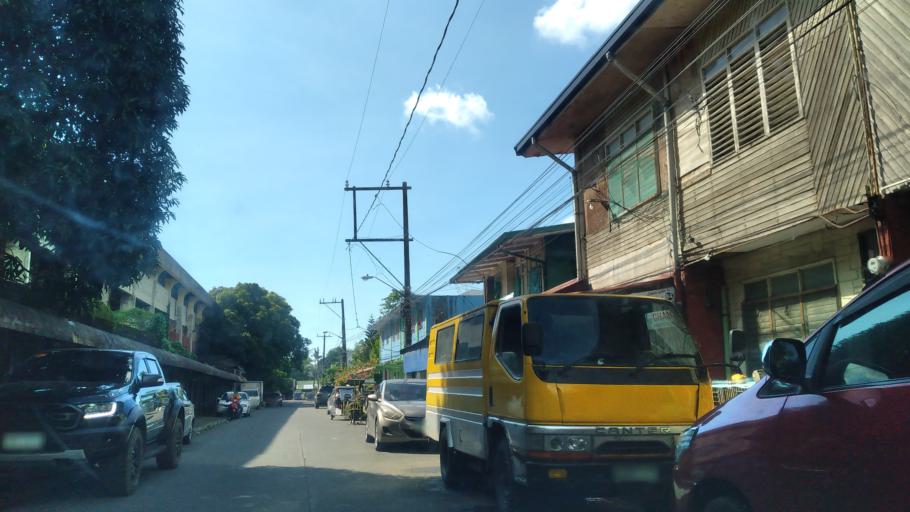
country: PH
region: Calabarzon
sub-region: Province of Quezon
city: Lucena
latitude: 13.9329
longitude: 121.6045
